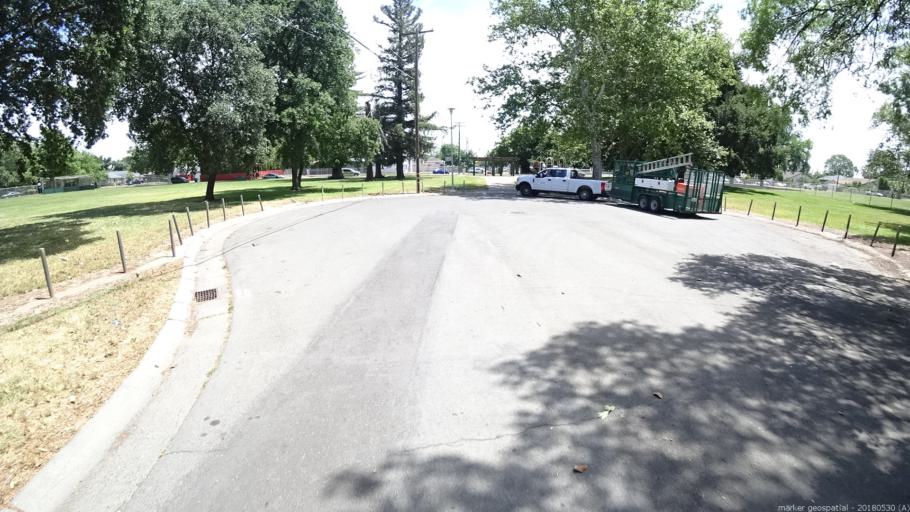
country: US
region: California
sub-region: Sacramento County
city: Rio Linda
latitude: 38.6349
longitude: -121.4559
